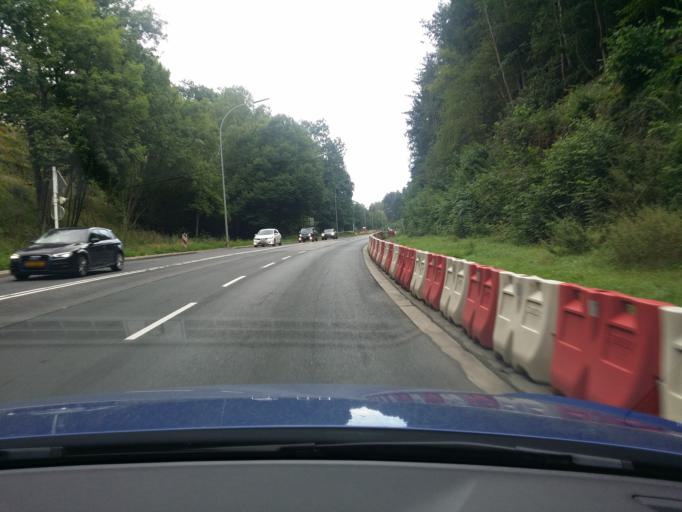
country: LU
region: Luxembourg
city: Kirchberg
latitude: 49.6104
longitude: 6.1525
